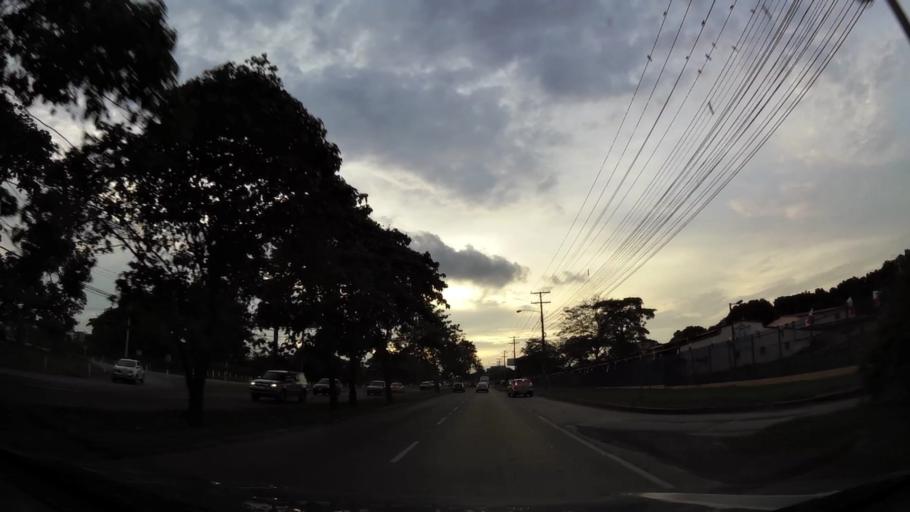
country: PA
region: Panama
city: Tocumen
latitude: 9.0696
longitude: -79.3974
